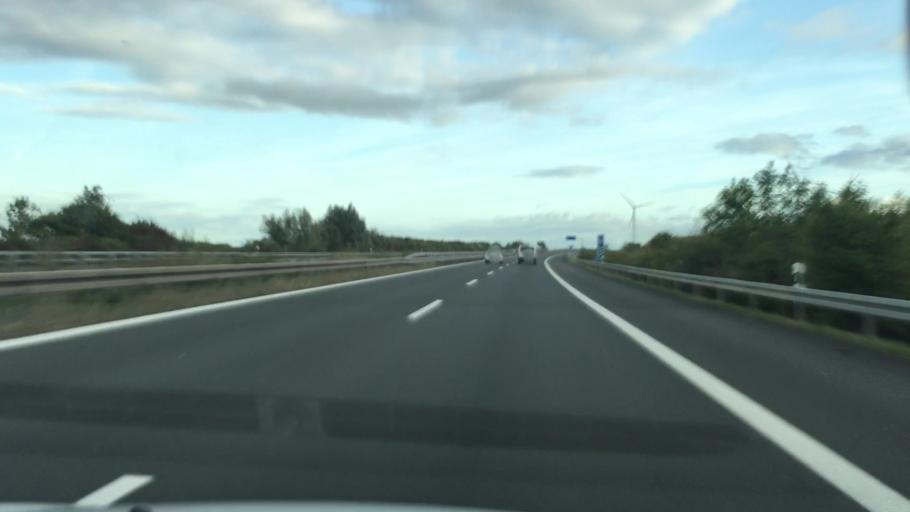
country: DE
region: Saxony-Anhalt
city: Nauendorf
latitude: 51.6364
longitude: 11.8516
